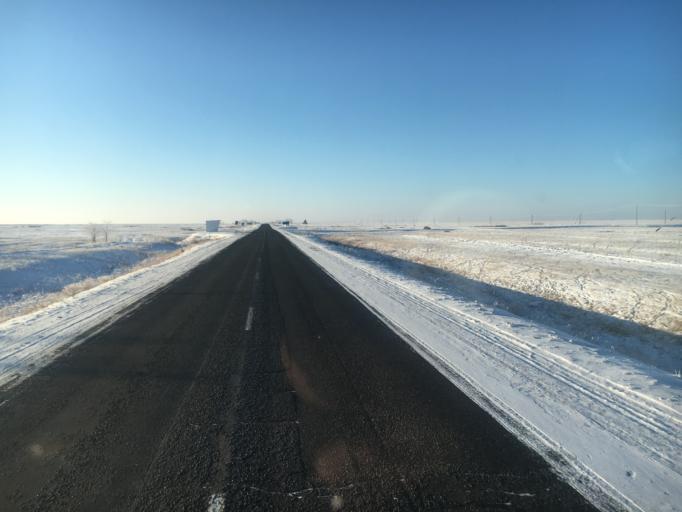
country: RU
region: Orenburg
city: Dombarovskiy
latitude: 50.1105
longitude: 59.3037
